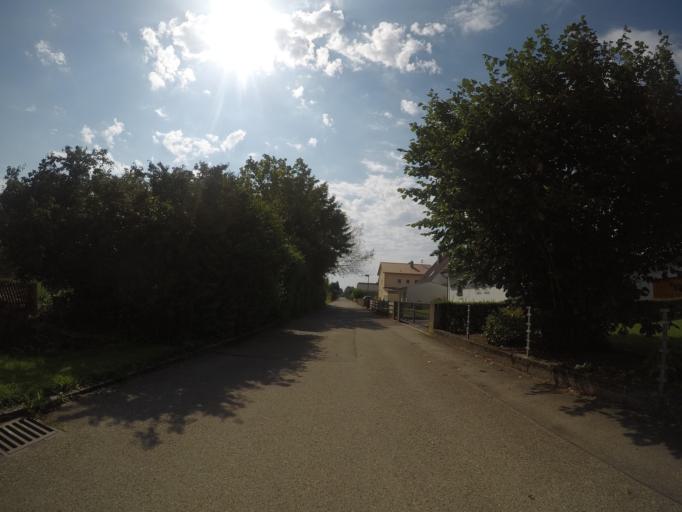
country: DE
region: Baden-Wuerttemberg
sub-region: Tuebingen Region
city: Kirchberg an der Iller
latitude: 48.1639
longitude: 10.0803
